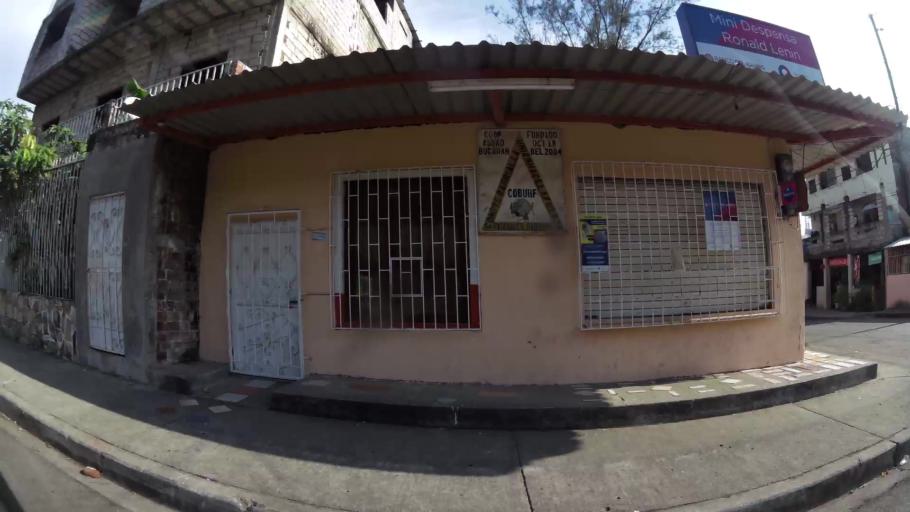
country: EC
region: Guayas
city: Eloy Alfaro
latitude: -2.0736
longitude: -79.9319
